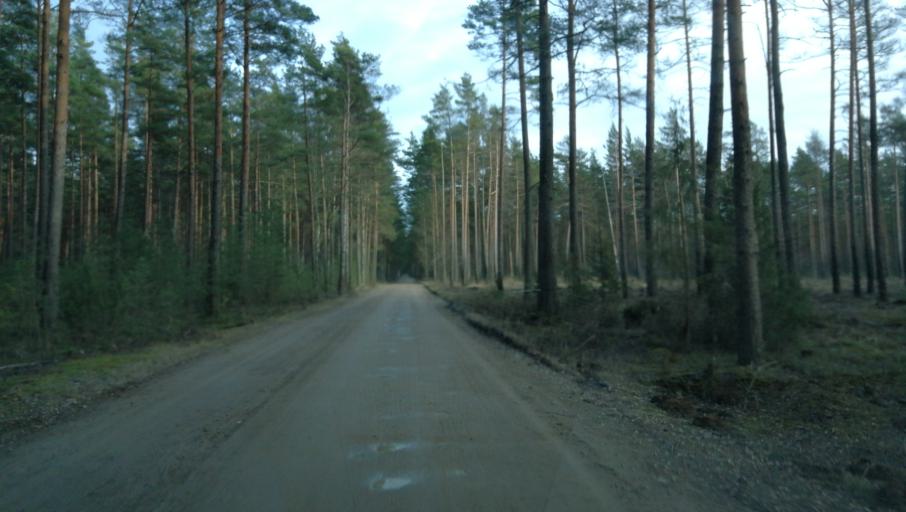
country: LV
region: Adazi
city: Adazi
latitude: 57.0531
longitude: 24.3056
